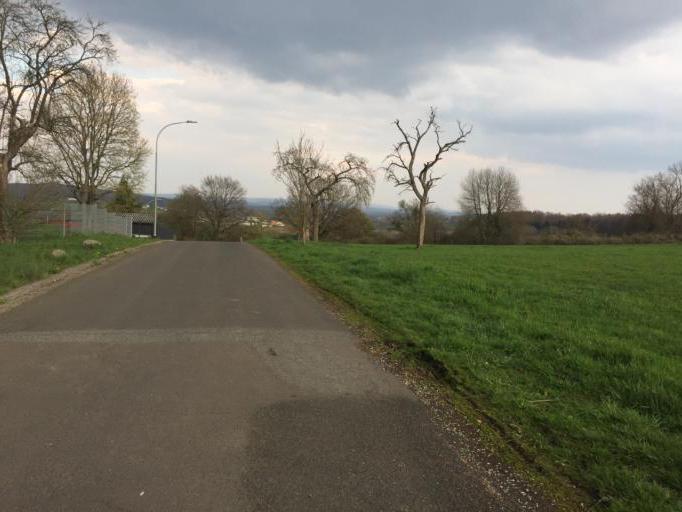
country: DE
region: Hesse
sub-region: Regierungsbezirk Giessen
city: Laubach
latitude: 50.5439
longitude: 8.9489
